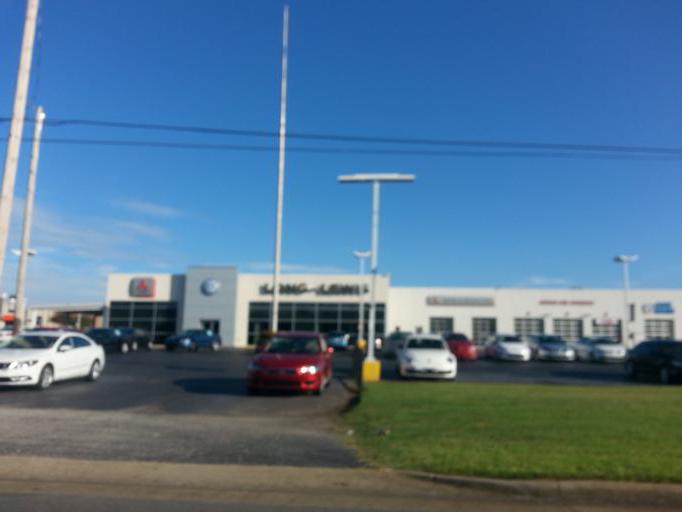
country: US
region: Alabama
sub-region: Lauderdale County
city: East Florence
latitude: 34.8211
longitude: -87.6531
